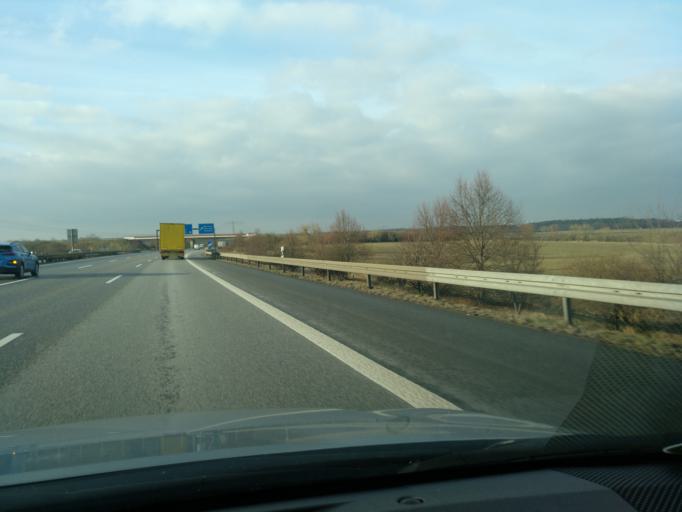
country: DE
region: Brandenburg
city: Woltersdorf
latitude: 52.4763
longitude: 13.7616
